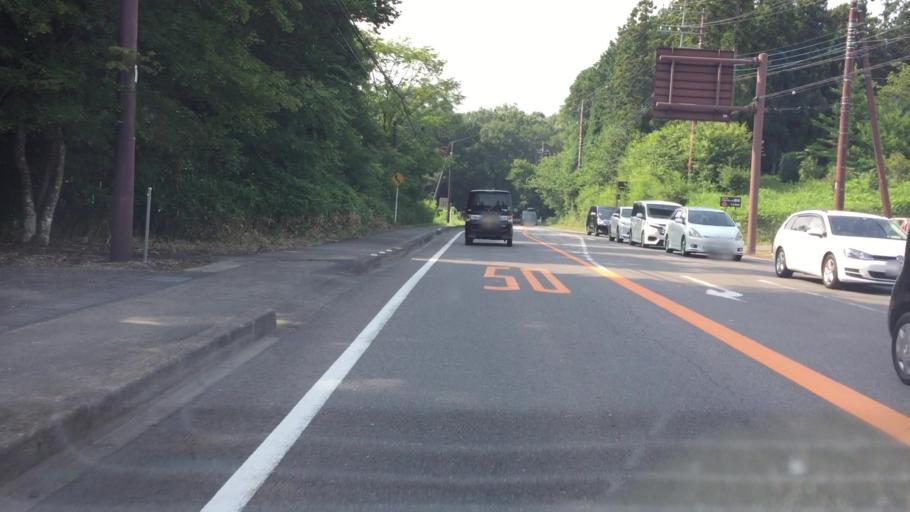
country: JP
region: Tochigi
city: Kuroiso
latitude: 37.0263
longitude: 140.0246
